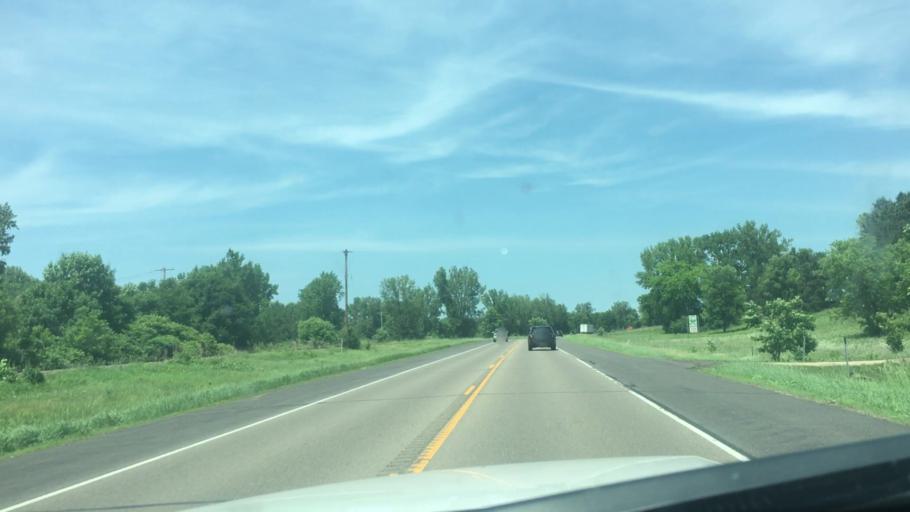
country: US
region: Minnesota
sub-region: Ramsey County
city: White Bear Lake
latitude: 45.1161
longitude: -93.0021
